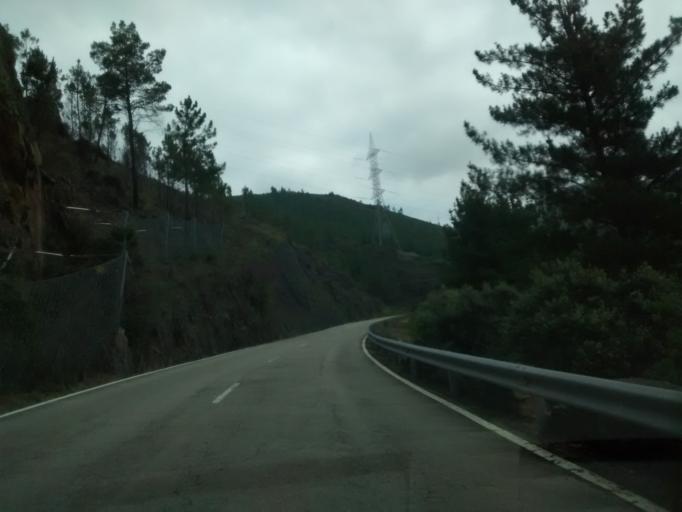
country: ES
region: Galicia
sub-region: Provincia de Ourense
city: Manzaneda
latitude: 42.3293
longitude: -7.2044
